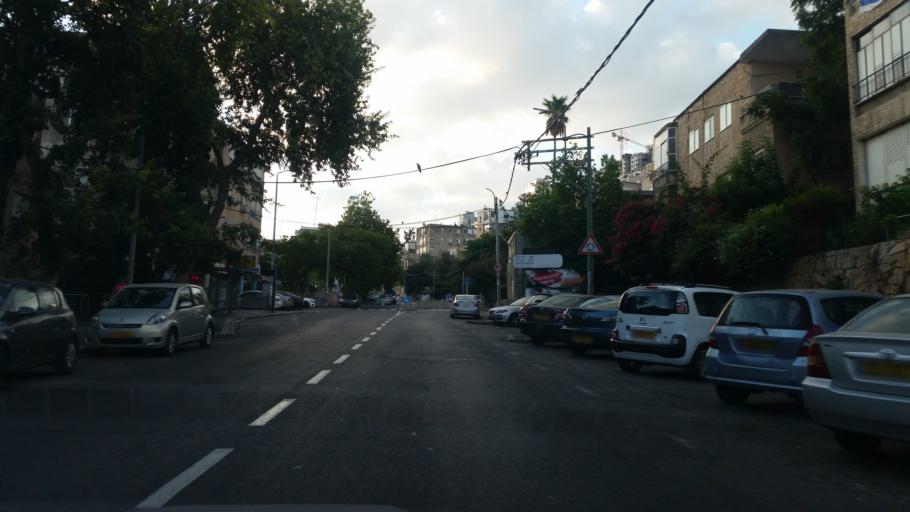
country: IL
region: Haifa
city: Haifa
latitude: 32.8004
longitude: 35.0116
